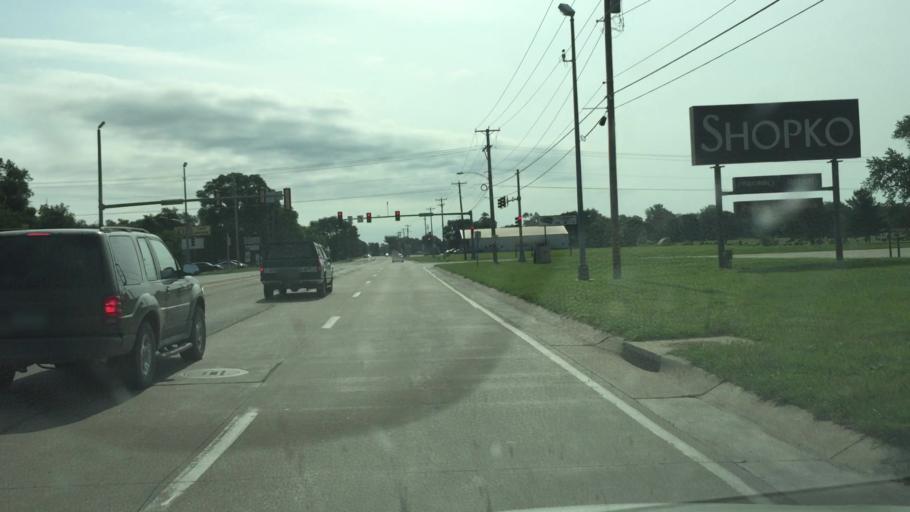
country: US
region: Iowa
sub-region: Lee County
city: Fort Madison
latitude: 40.6239
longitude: -91.3743
